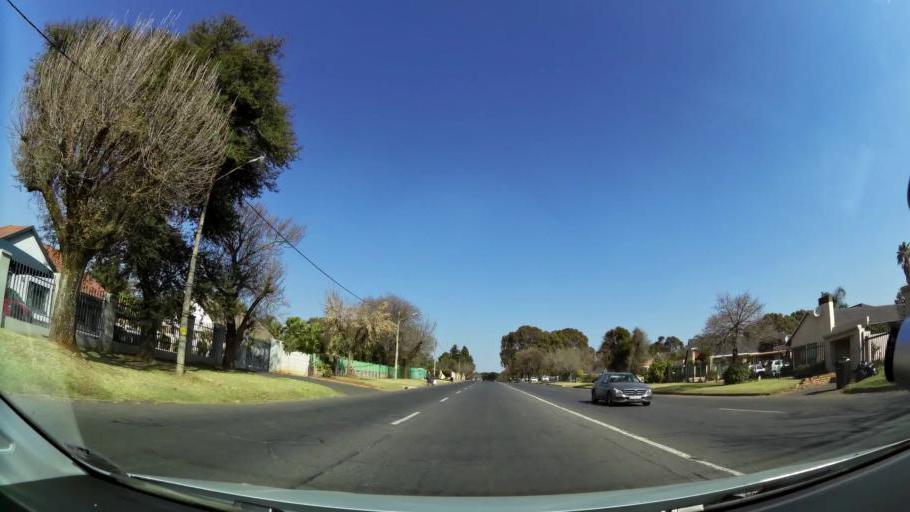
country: ZA
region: Gauteng
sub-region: City of Johannesburg Metropolitan Municipality
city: Modderfontein
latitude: -26.1179
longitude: 28.2331
